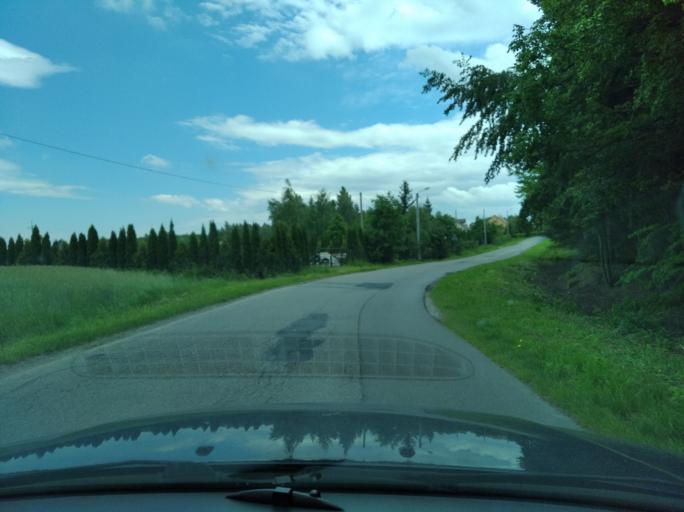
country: PL
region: Subcarpathian Voivodeship
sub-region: Powiat ropczycko-sedziszowski
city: Ropczyce
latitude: 50.0152
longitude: 21.6105
